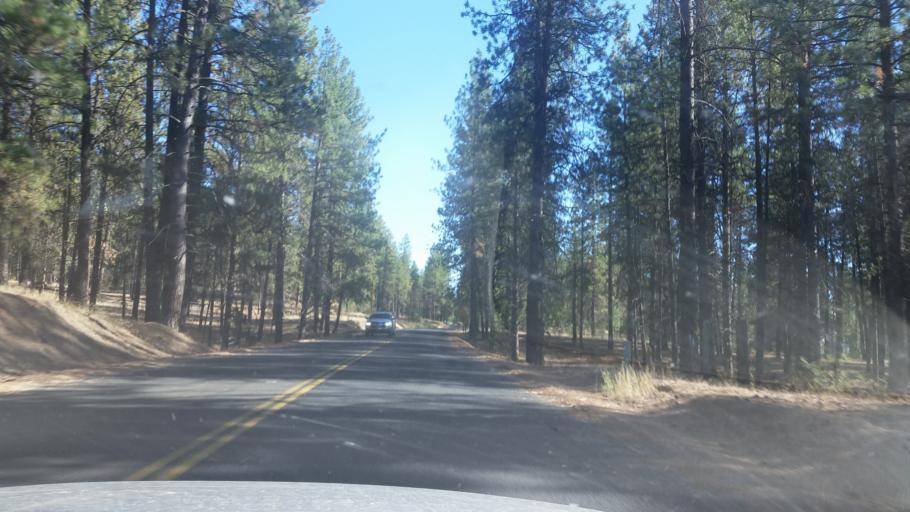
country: US
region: Washington
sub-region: Spokane County
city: Cheney
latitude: 47.5547
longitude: -117.4868
